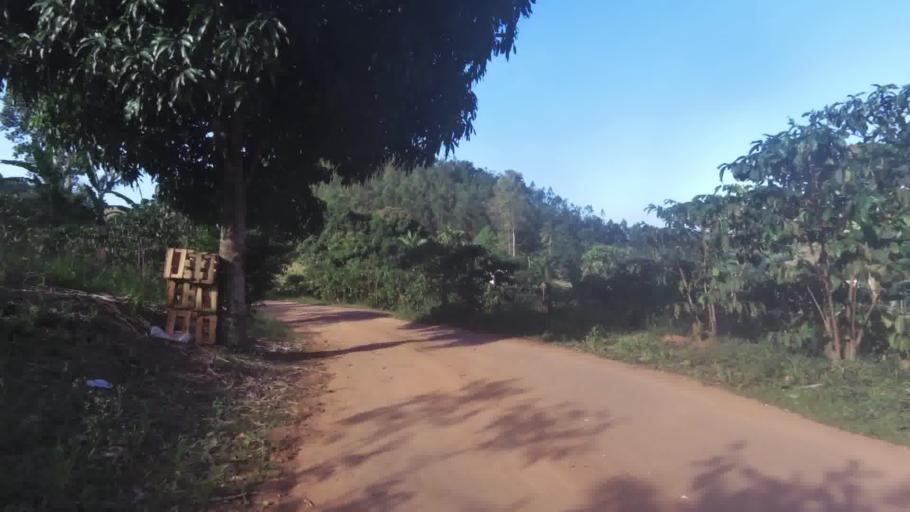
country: BR
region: Espirito Santo
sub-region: Iconha
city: Iconha
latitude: -20.7460
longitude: -40.7978
